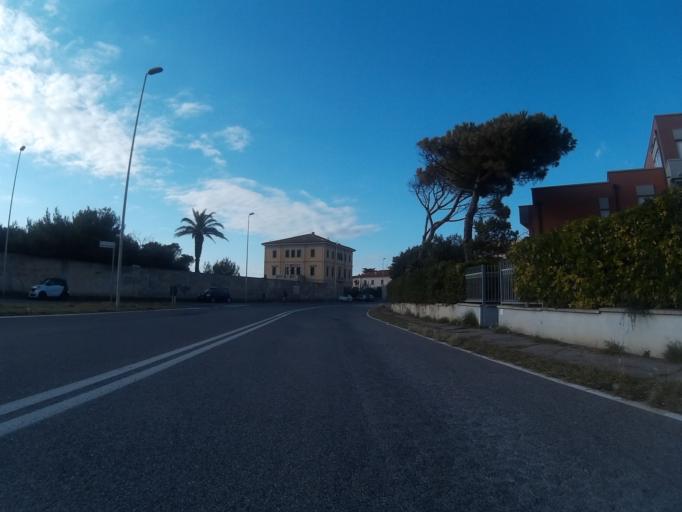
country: IT
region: Tuscany
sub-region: Provincia di Livorno
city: Quercianella
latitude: 43.4905
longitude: 10.3268
